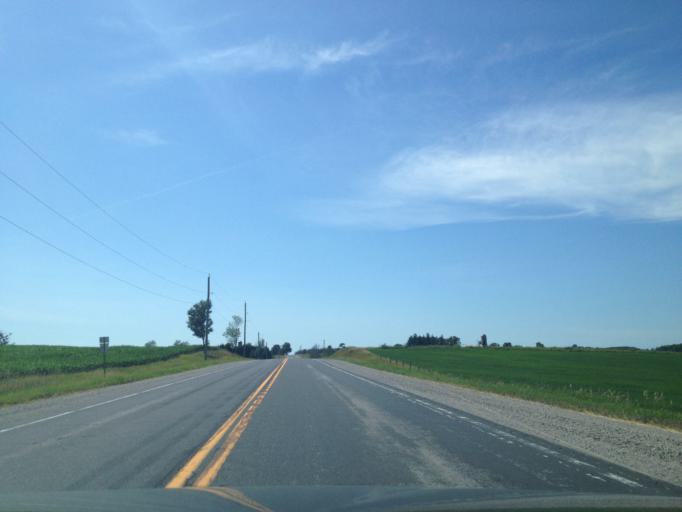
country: CA
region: Ontario
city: Stratford
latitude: 43.4862
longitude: -80.8402
